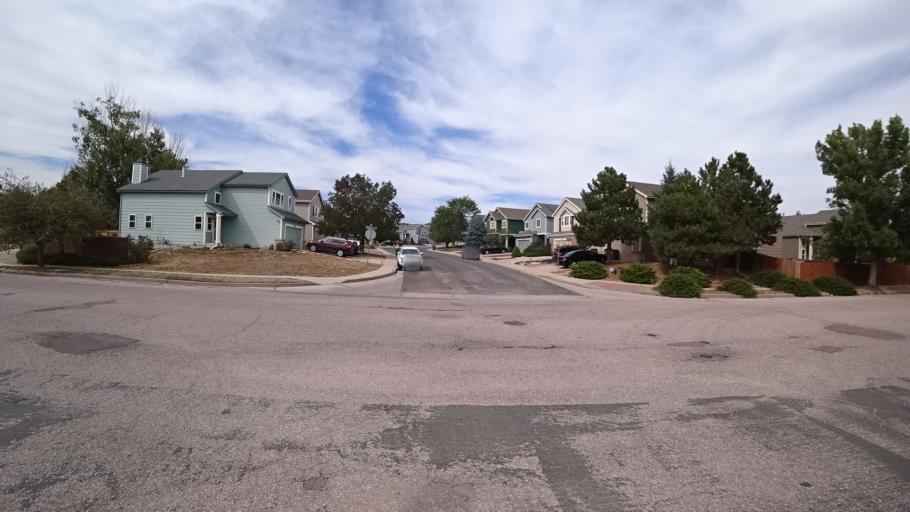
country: US
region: Colorado
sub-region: El Paso County
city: Cimarron Hills
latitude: 38.9061
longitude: -104.7067
